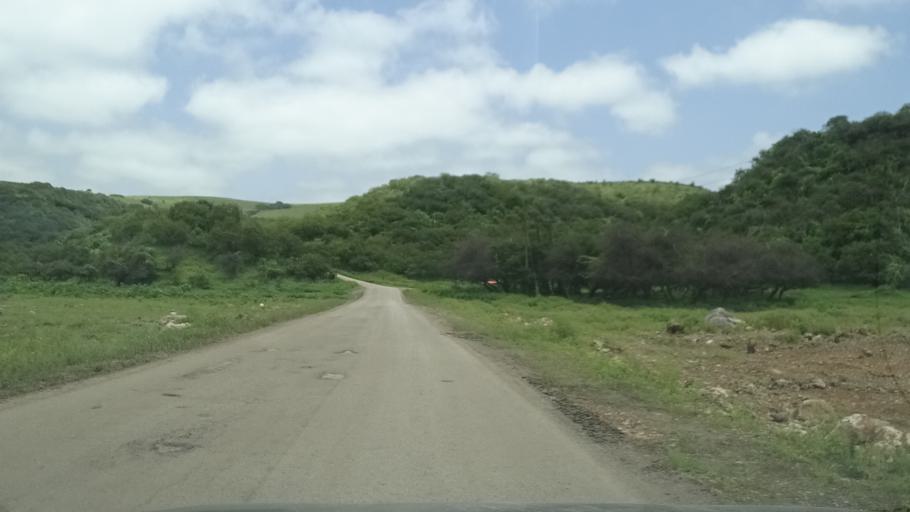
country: OM
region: Zufar
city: Salalah
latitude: 17.1982
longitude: 54.1815
